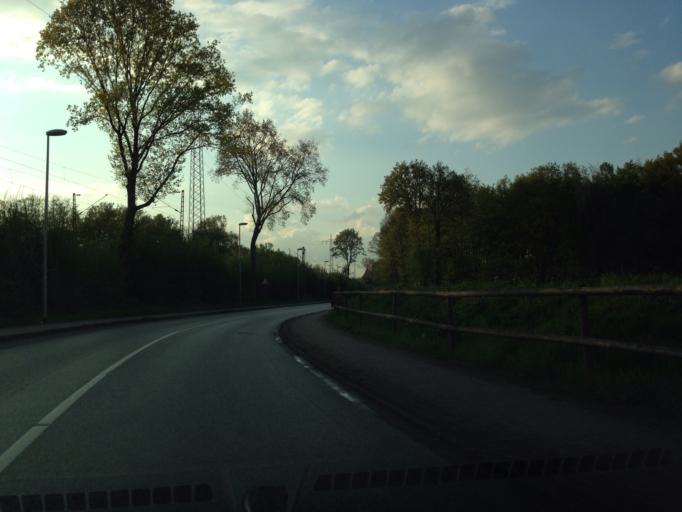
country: DE
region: North Rhine-Westphalia
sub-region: Regierungsbezirk Munster
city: Muenster
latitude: 51.9772
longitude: 7.6786
